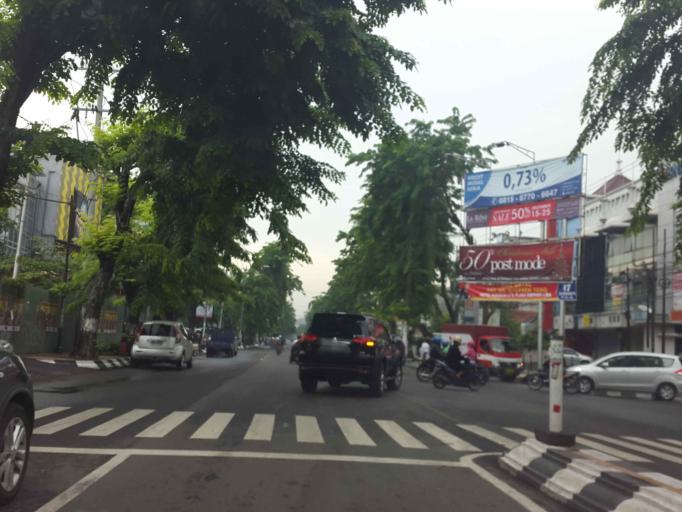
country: ID
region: Central Java
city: Semarang
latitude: -6.9821
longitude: 110.4216
